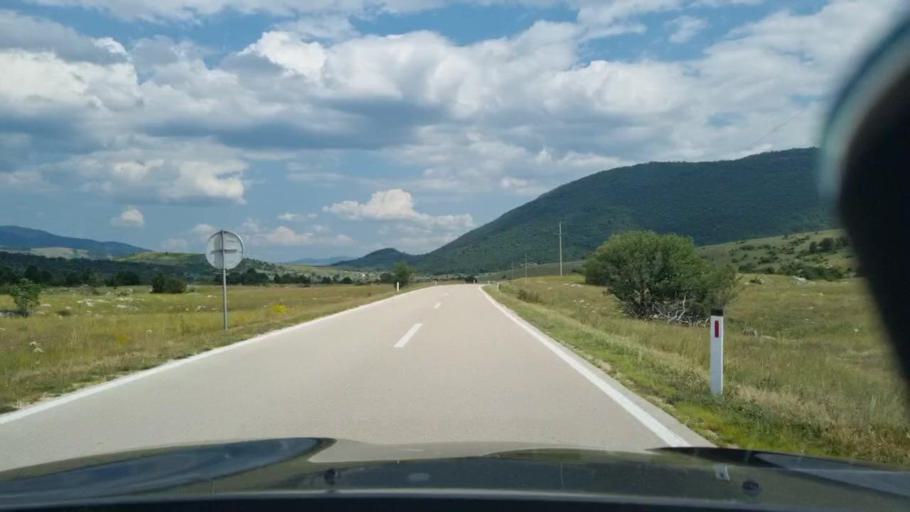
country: BA
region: Federation of Bosnia and Herzegovina
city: Bosansko Grahovo
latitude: 44.1420
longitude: 16.4665
